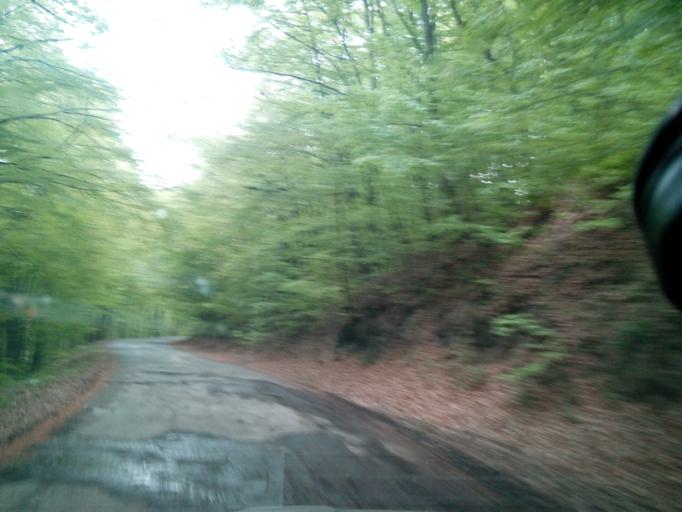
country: SK
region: Kosicky
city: Secovce
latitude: 48.8122
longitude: 21.5199
